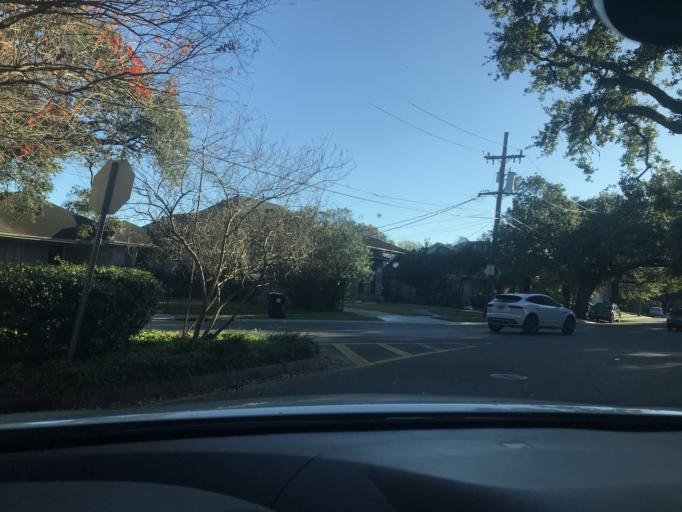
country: US
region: Louisiana
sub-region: Orleans Parish
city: New Orleans
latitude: 29.9560
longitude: -90.1068
